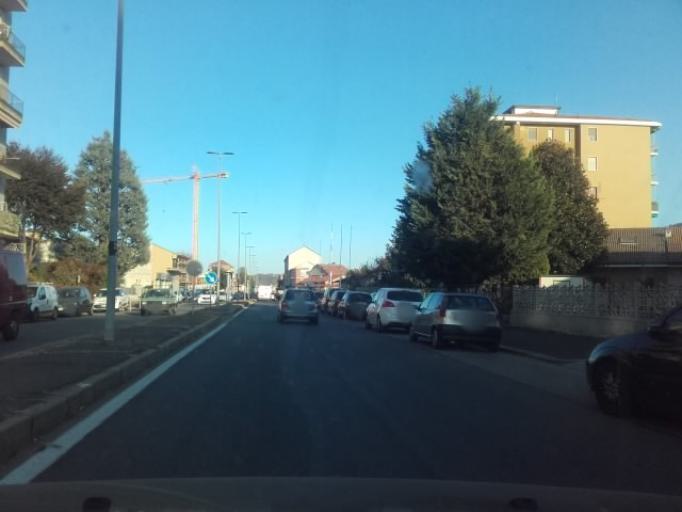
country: IT
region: Piedmont
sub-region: Provincia di Torino
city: San Mauro Torinese
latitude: 45.1000
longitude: 7.7279
